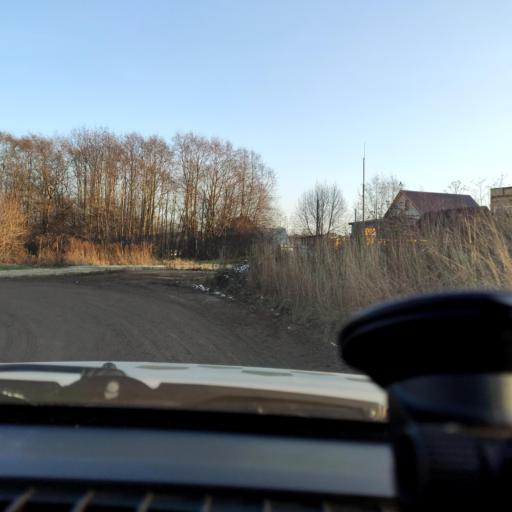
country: RU
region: Perm
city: Ferma
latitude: 57.9461
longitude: 56.3549
